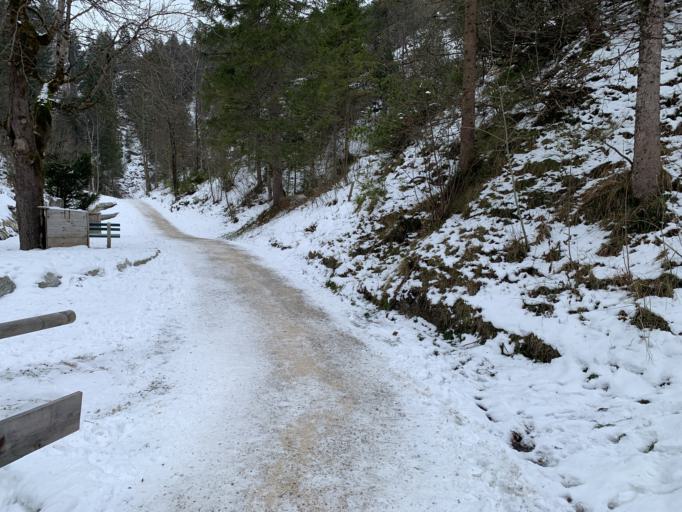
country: DE
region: Bavaria
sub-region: Upper Bavaria
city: Mittenwald
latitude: 47.4400
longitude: 11.2504
